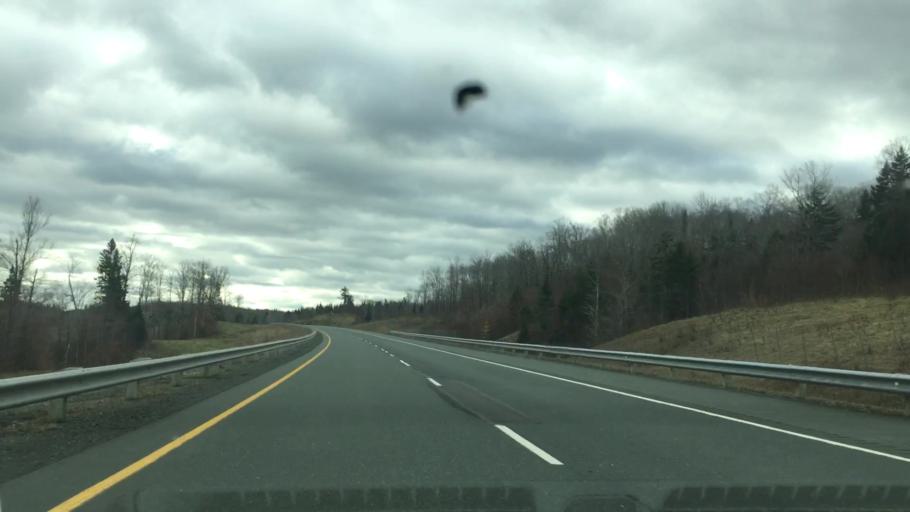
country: US
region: Maine
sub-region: Aroostook County
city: Fort Fairfield
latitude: 46.6461
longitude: -67.7435
